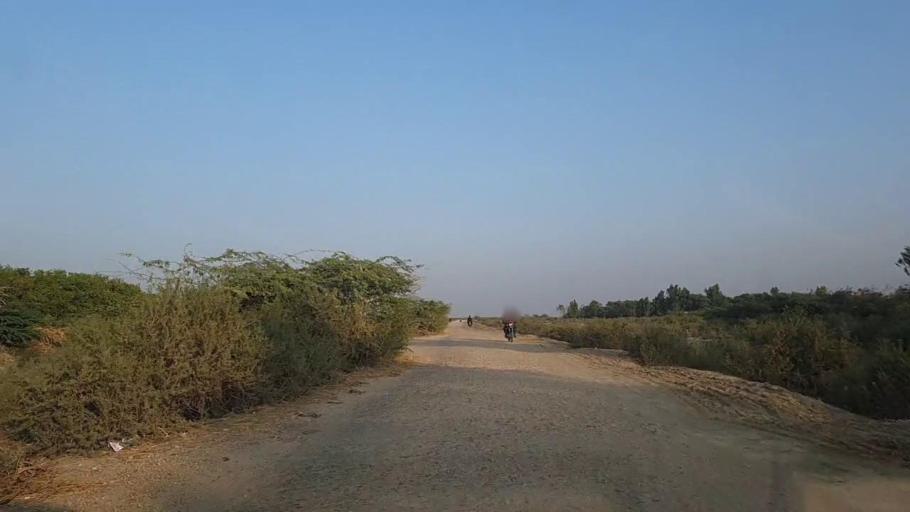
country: PK
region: Sindh
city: Keti Bandar
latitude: 24.2718
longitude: 67.6778
